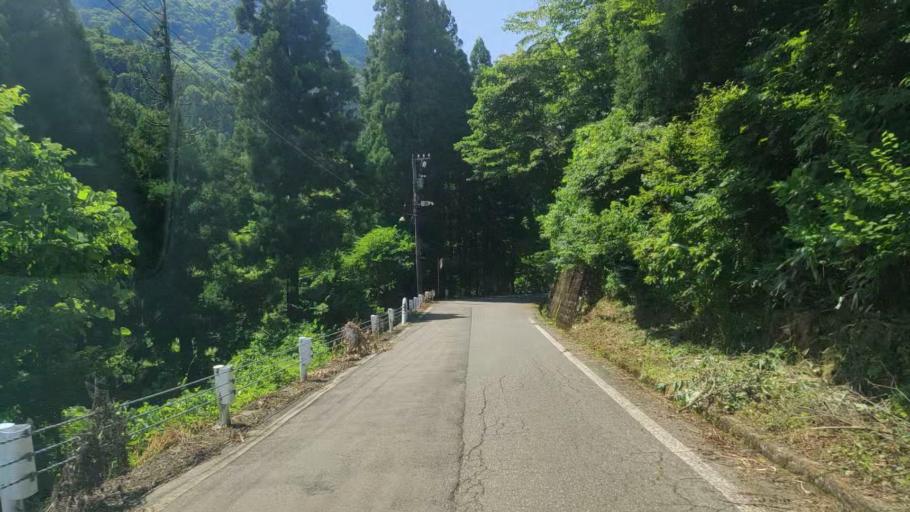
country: JP
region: Fukui
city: Katsuyama
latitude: 36.1195
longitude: 136.5083
